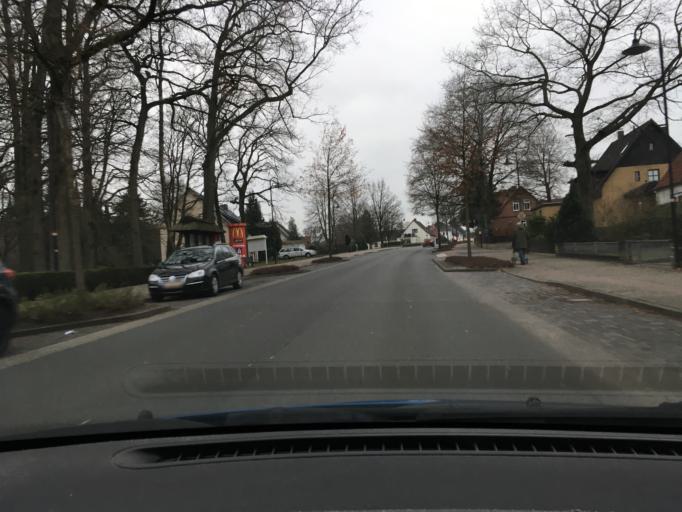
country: DE
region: Lower Saxony
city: Bad Fallingbostel
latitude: 52.8646
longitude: 9.6903
